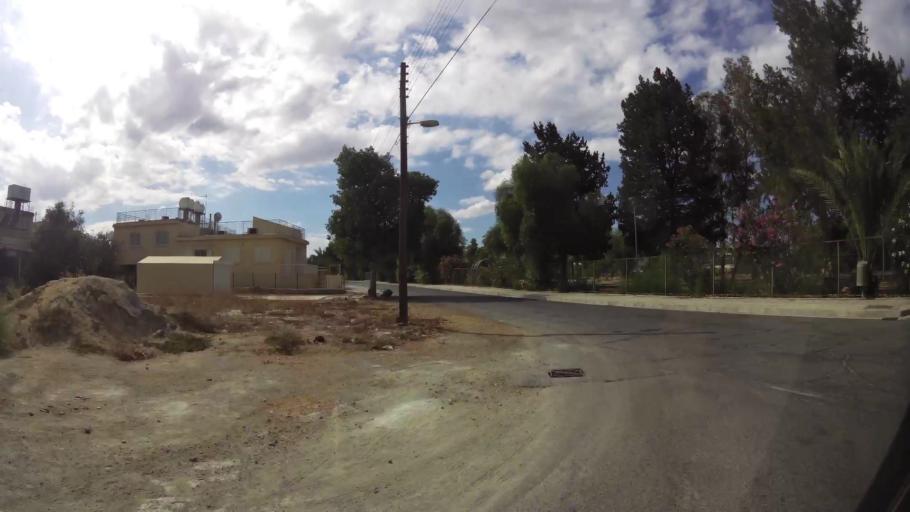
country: CY
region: Lefkosia
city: Nicosia
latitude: 35.1923
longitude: 33.3902
